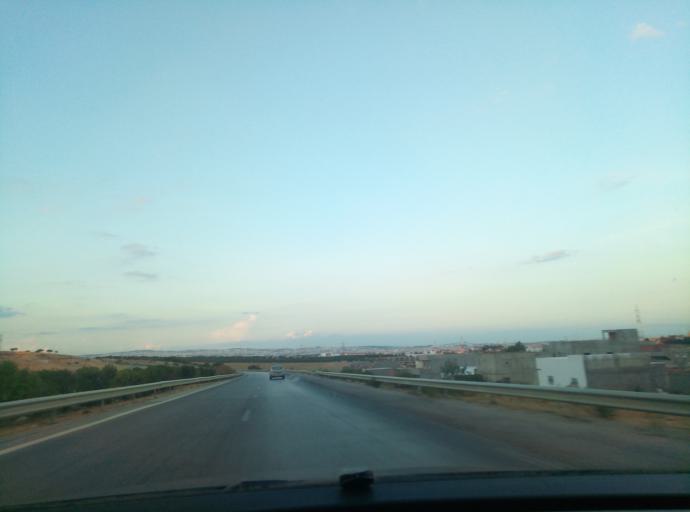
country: TN
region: Manouba
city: Manouba
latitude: 36.7652
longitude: 10.0682
